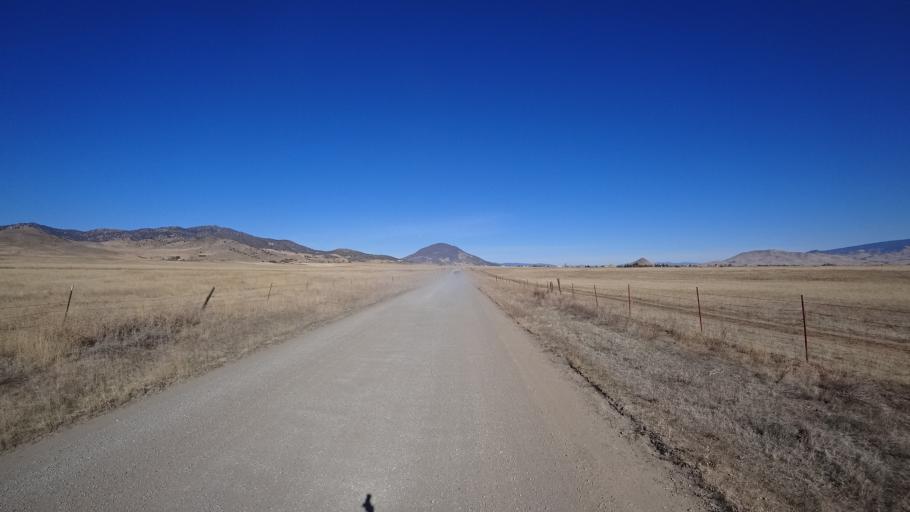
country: US
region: California
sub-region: Siskiyou County
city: Montague
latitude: 41.7735
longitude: -122.5053
